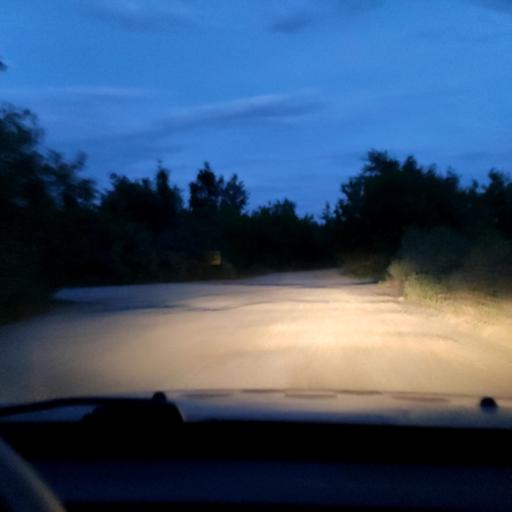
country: RU
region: Perm
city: Kondratovo
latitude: 58.0301
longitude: 56.0624
